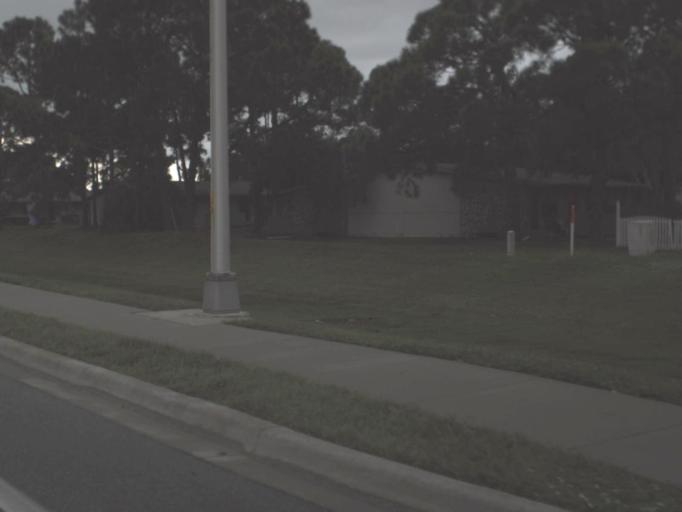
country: US
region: Florida
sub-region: Sarasota County
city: North Sarasota
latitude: 27.3762
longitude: -82.5310
